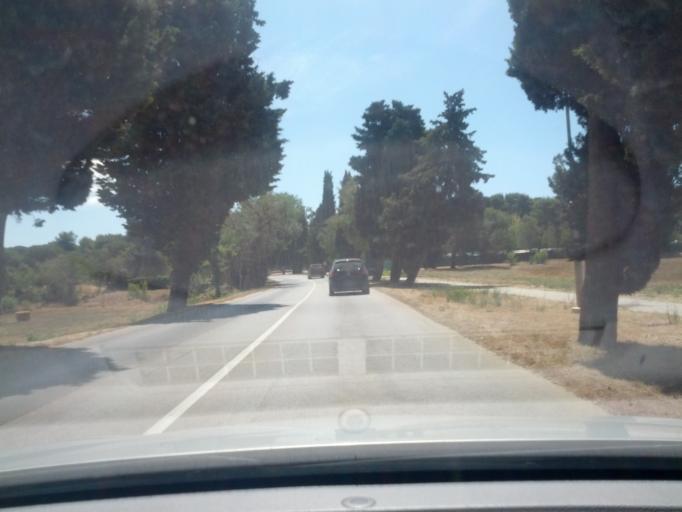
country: HR
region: Istarska
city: Fazana
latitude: 44.9211
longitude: 13.8079
